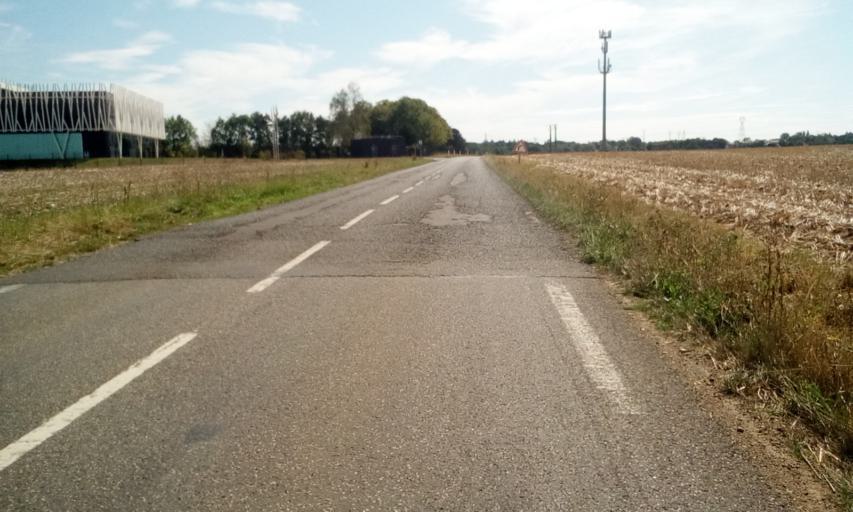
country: FR
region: Lower Normandy
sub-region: Departement du Calvados
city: Eterville
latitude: 49.1413
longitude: -0.4060
